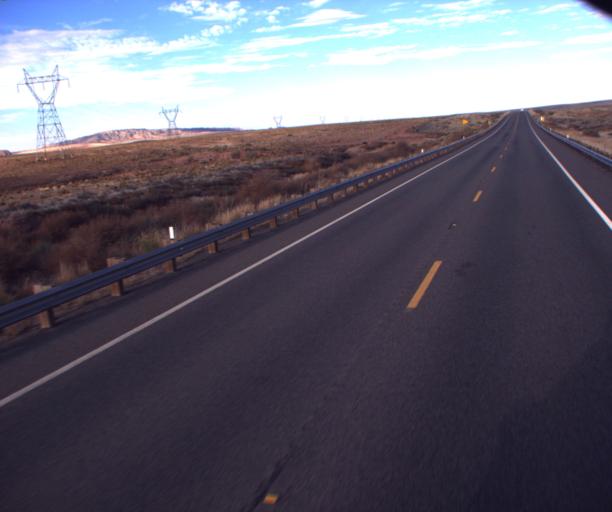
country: US
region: Arizona
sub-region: Apache County
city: Lukachukai
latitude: 36.9373
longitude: -109.2407
